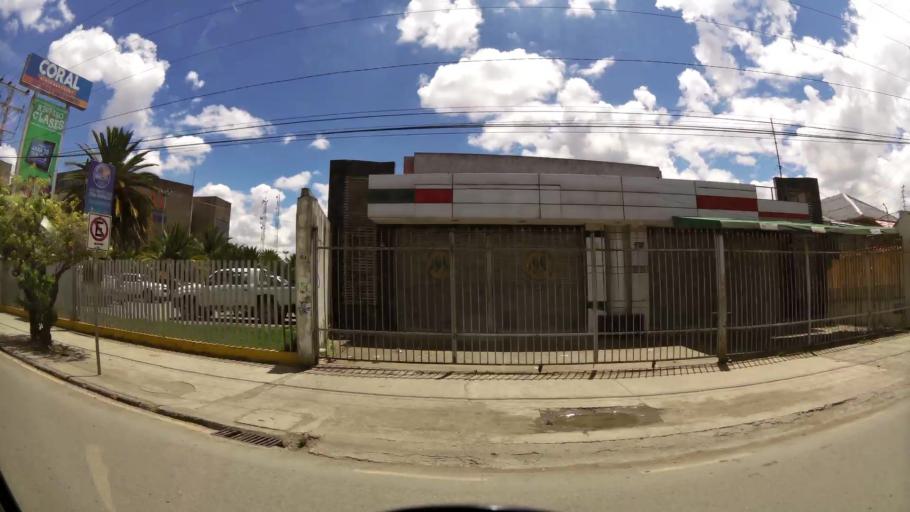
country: EC
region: Azuay
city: Cuenca
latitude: -2.9169
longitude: -79.0387
